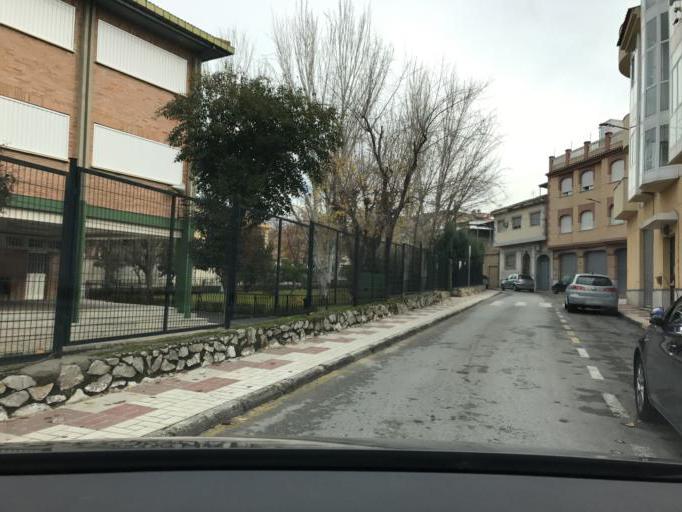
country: ES
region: Andalusia
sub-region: Provincia de Granada
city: Maracena
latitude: 37.2104
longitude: -3.6347
